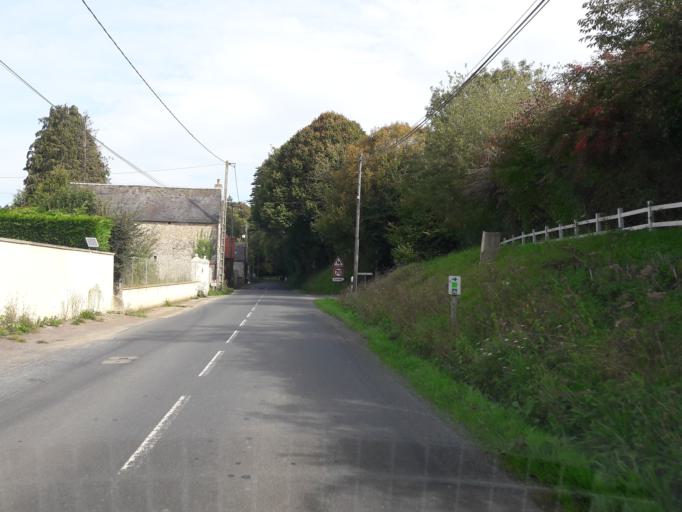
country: FR
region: Lower Normandy
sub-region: Departement du Calvados
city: Bayeux
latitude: 49.2169
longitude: -0.7111
